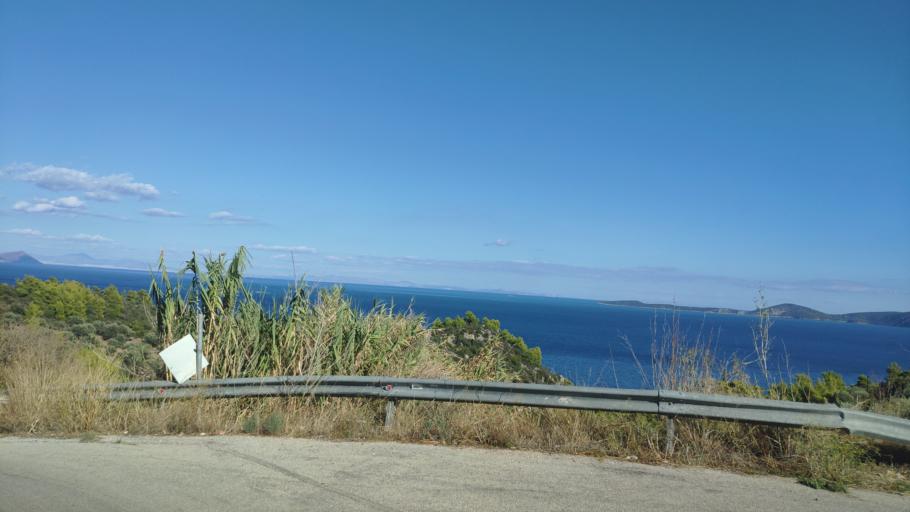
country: GR
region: Attica
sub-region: Nomos Piraios
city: Galatas
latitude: 37.5455
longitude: 23.3779
